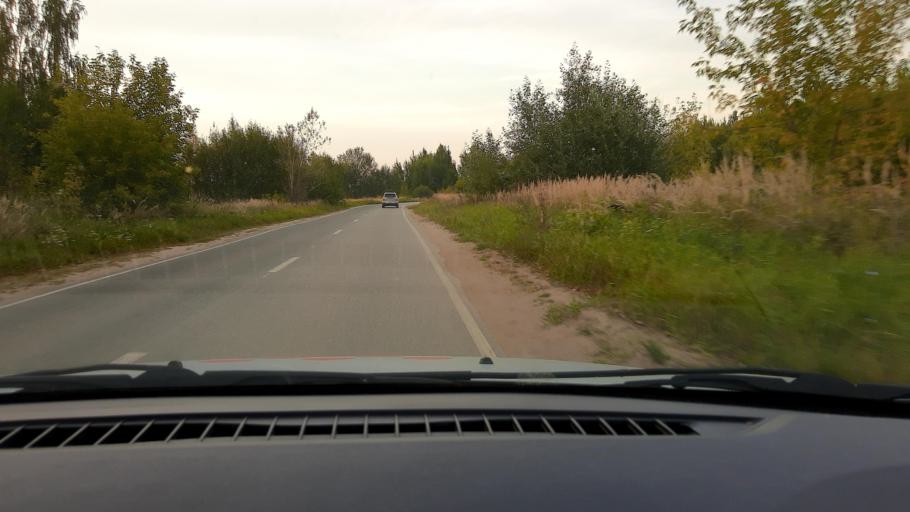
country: RU
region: Nizjnij Novgorod
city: Bor
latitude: 56.3433
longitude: 44.0466
